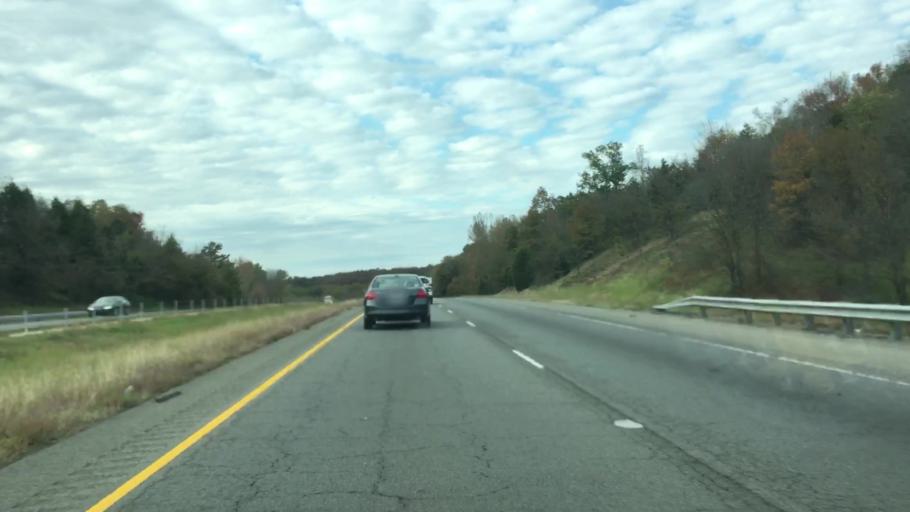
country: US
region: Arkansas
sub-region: Faulkner County
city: Conway
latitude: 35.1345
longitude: -92.5185
